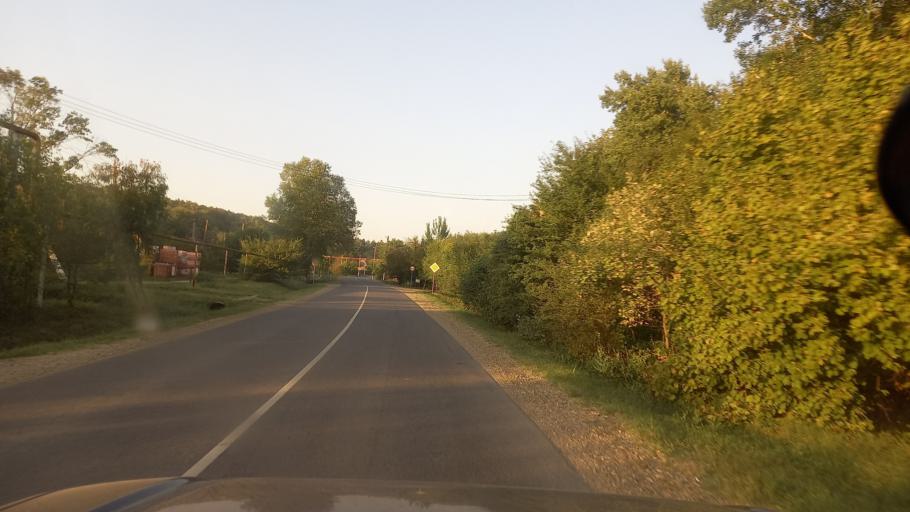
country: RU
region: Krasnodarskiy
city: Smolenskaya
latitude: 44.7662
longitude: 38.7785
